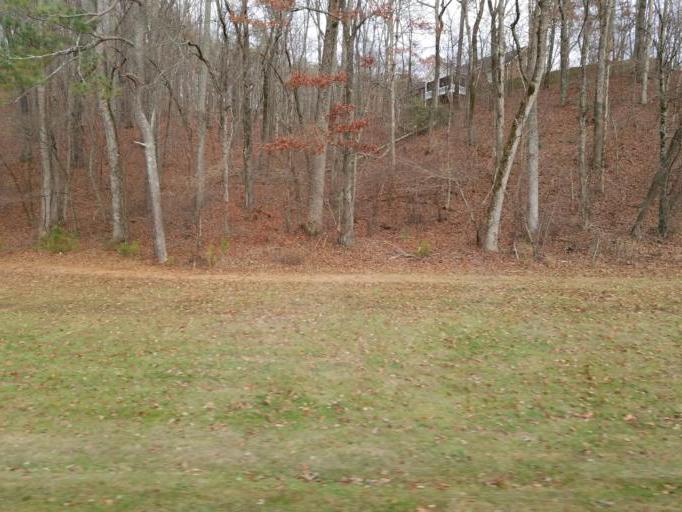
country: US
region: Georgia
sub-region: Pickens County
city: Jasper
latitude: 34.5104
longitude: -84.4421
